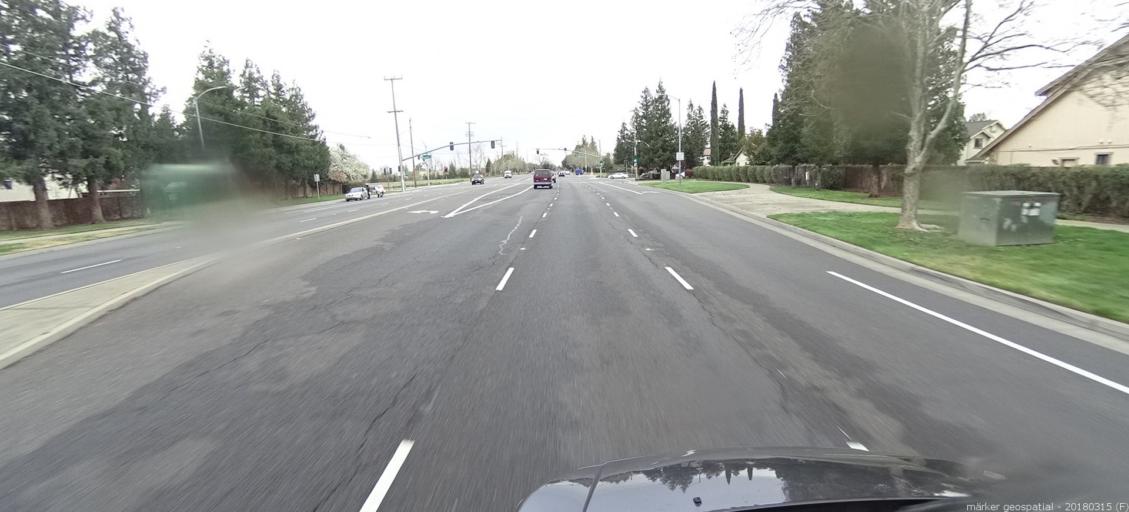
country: US
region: California
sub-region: Sacramento County
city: Laguna
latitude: 38.4330
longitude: -121.4464
